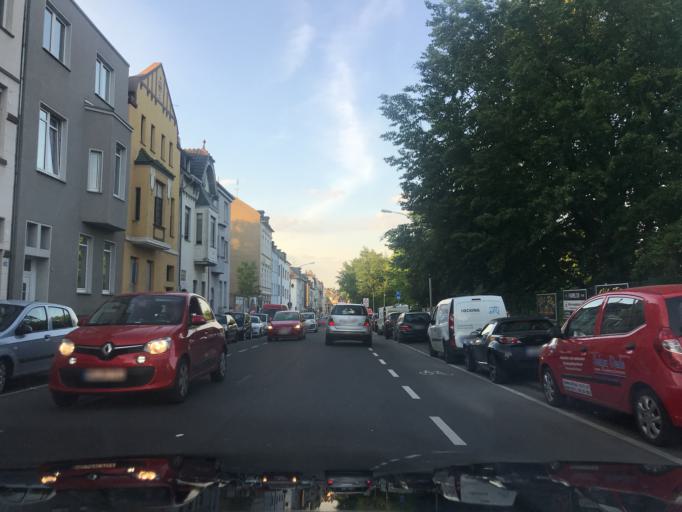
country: DE
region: North Rhine-Westphalia
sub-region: Regierungsbezirk Dusseldorf
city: Monchengladbach
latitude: 51.1891
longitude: 6.4199
